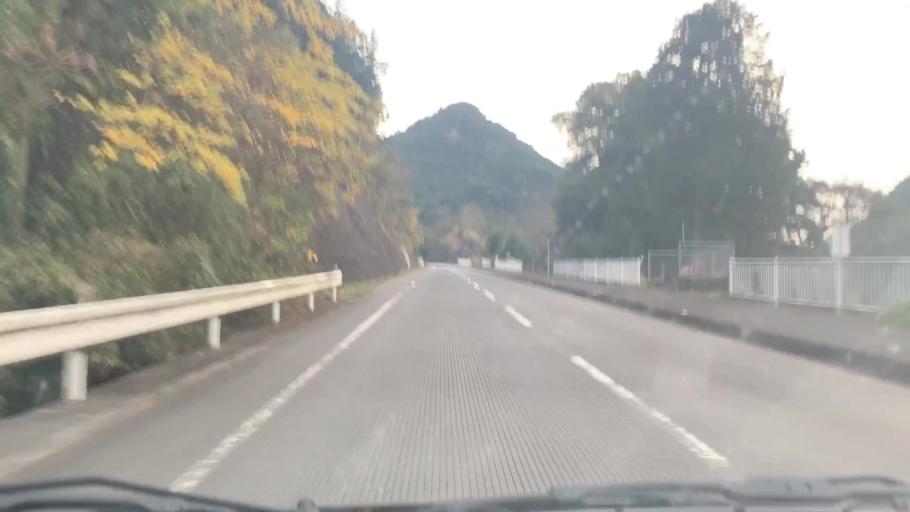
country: JP
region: Saga Prefecture
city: Kashima
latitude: 33.0535
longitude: 130.0722
